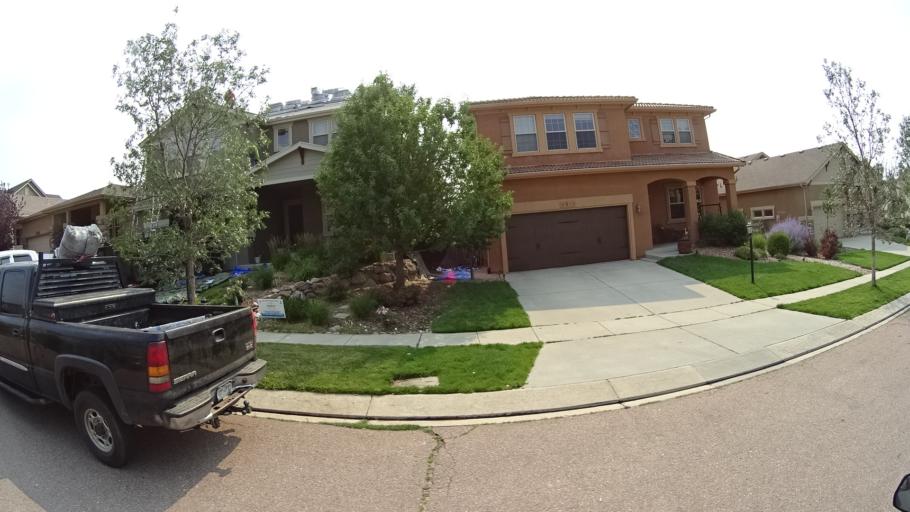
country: US
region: Colorado
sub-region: El Paso County
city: Black Forest
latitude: 38.9697
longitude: -104.7330
